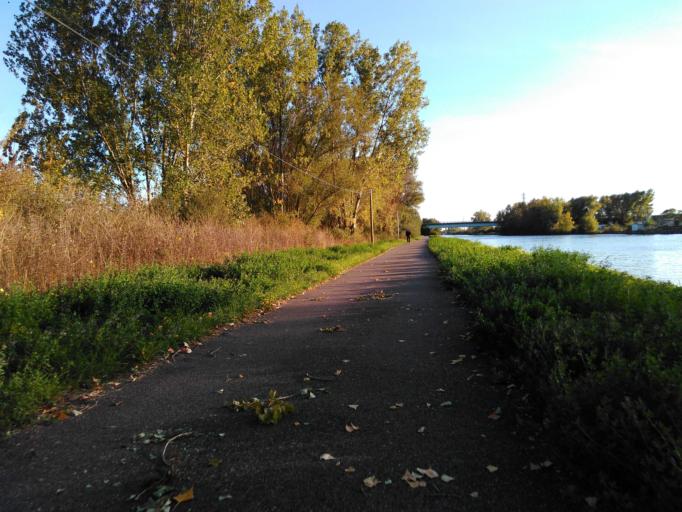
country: FR
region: Lorraine
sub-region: Departement de la Moselle
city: Talange
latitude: 49.2216
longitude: 6.1830
